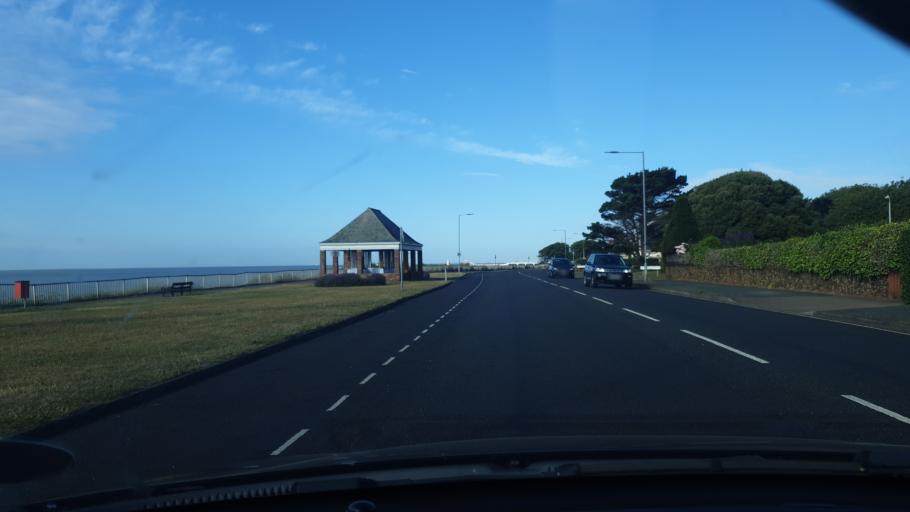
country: GB
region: England
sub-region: Essex
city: Clacton-on-Sea
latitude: 51.7932
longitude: 1.1691
